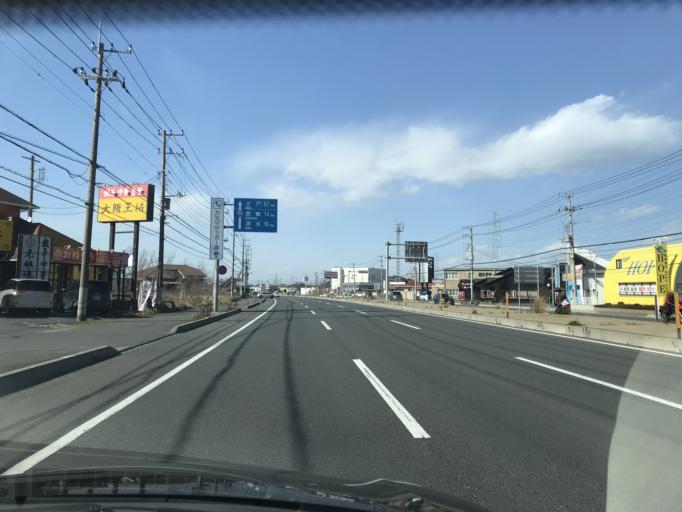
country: JP
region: Chiba
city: Omigawa
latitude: 35.8778
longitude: 140.6863
